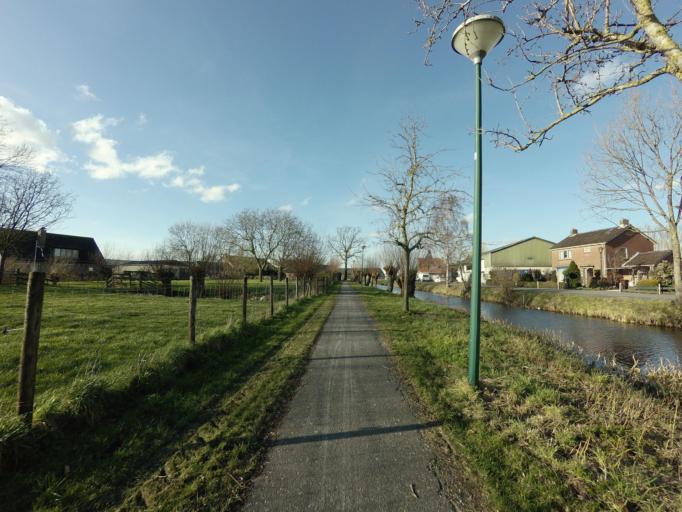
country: NL
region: Utrecht
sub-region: Gemeente Lopik
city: Lopik
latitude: 51.9837
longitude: 4.9974
